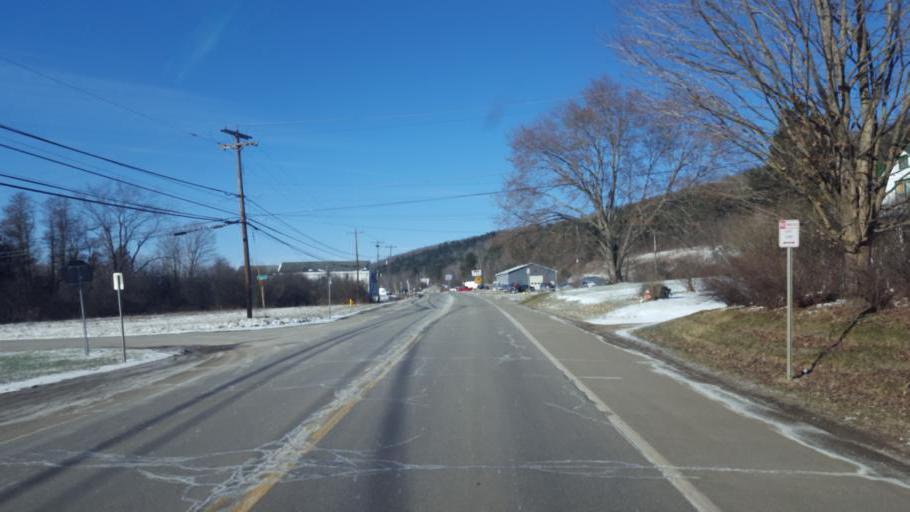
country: US
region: New York
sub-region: Allegany County
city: Wellsville
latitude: 42.1325
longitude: -77.9174
